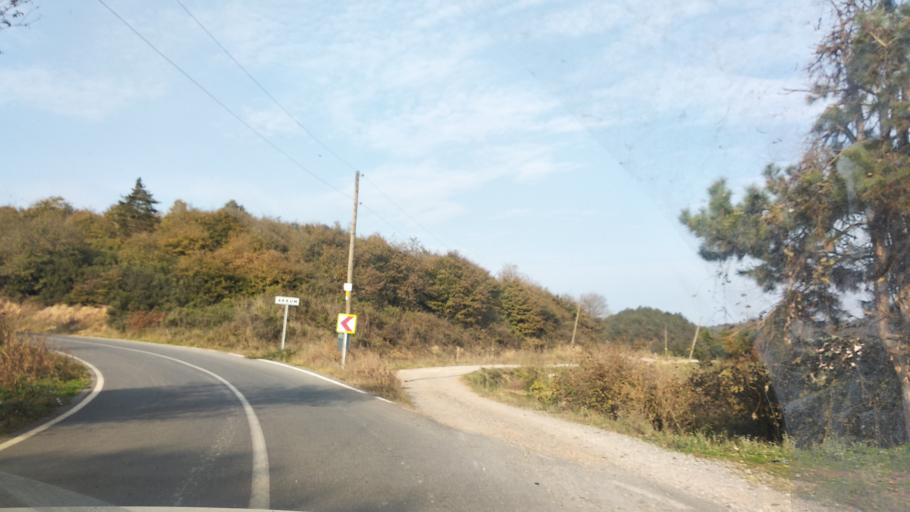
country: TR
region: Sakarya
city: Karasu
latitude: 41.0643
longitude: 30.6183
